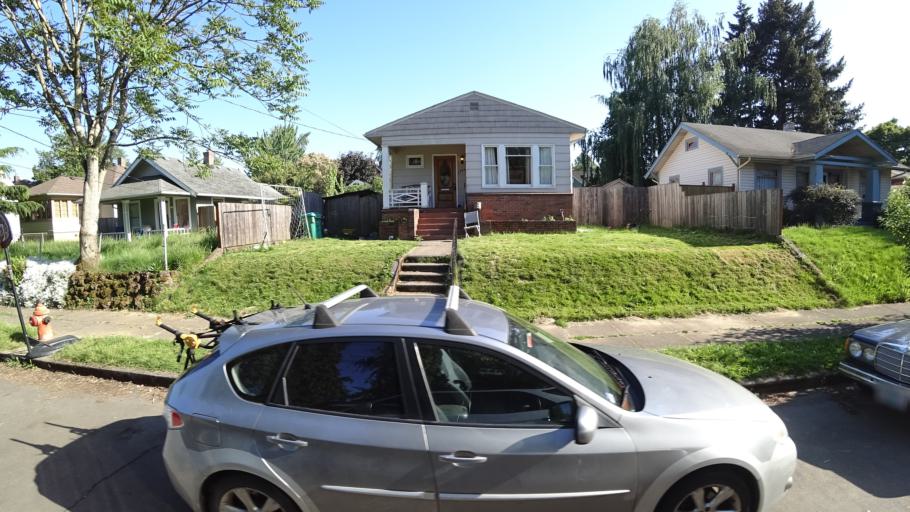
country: US
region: Oregon
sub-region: Multnomah County
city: Portland
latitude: 45.5554
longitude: -122.6859
